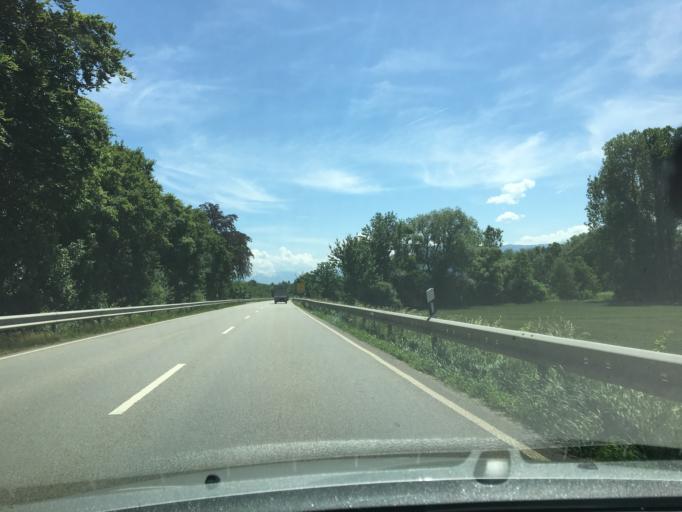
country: DE
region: Bavaria
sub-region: Upper Bavaria
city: Freilassing
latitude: 47.8852
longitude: 12.9666
